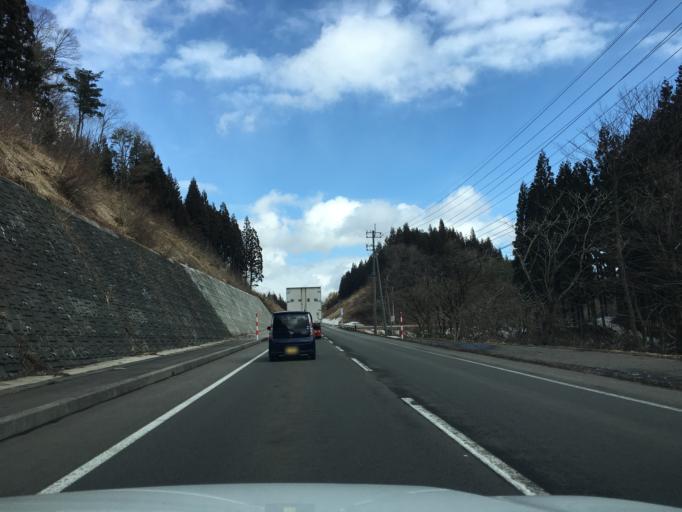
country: JP
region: Akita
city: Takanosu
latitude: 40.1016
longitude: 140.3464
